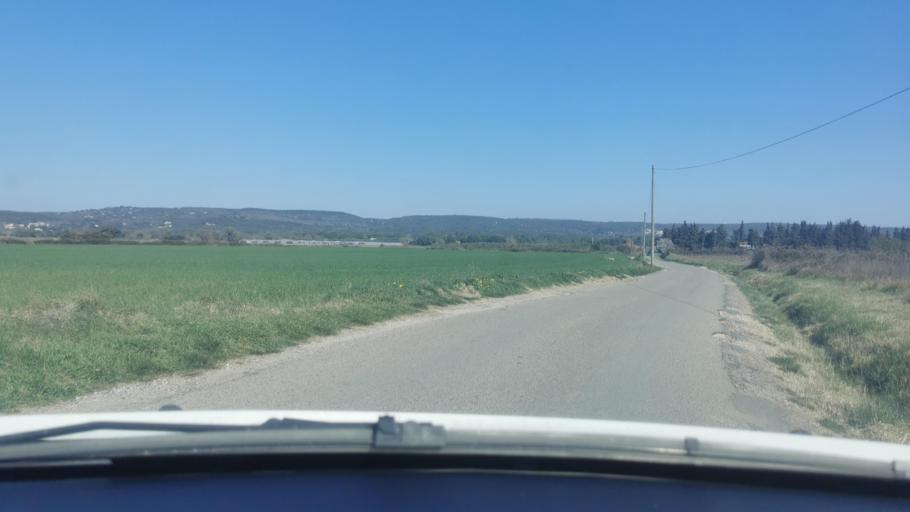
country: FR
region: Languedoc-Roussillon
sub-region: Departement du Gard
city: Montaren-et-Saint-Mediers
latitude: 44.0354
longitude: 4.3892
